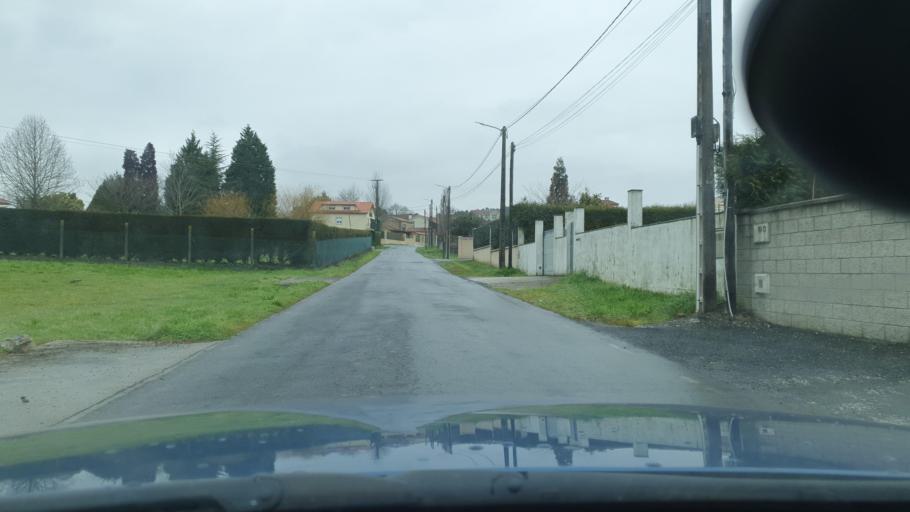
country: ES
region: Galicia
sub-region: Provincia da Coruna
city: Ames
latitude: 42.8316
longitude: -8.6072
